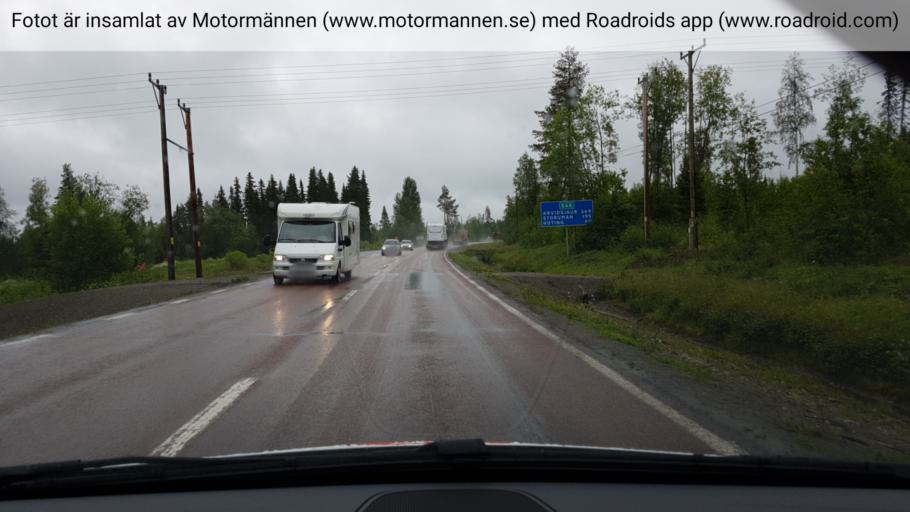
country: SE
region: Jaemtland
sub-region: Stroemsunds Kommun
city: Stroemsund
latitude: 63.8609
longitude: 15.5676
